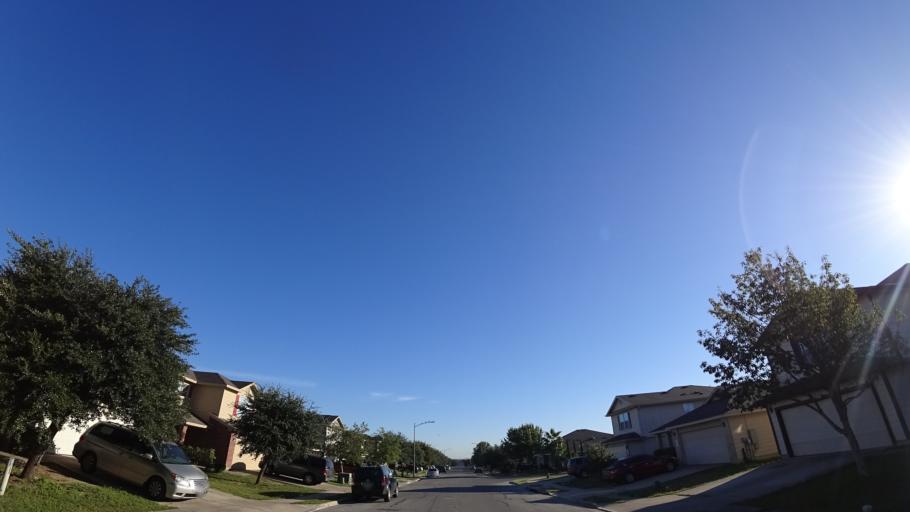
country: US
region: Texas
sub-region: Travis County
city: Austin
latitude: 30.2234
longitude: -97.6943
